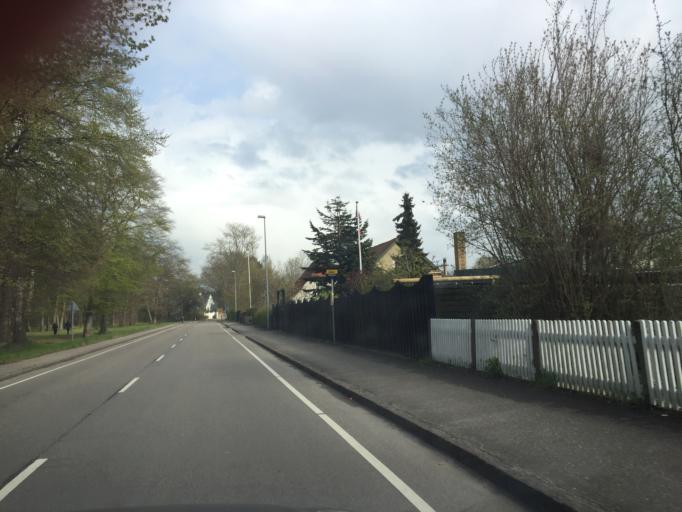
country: DK
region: Capital Region
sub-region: Halsnaes Kommune
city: Liseleje
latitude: 56.0123
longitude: 11.9725
